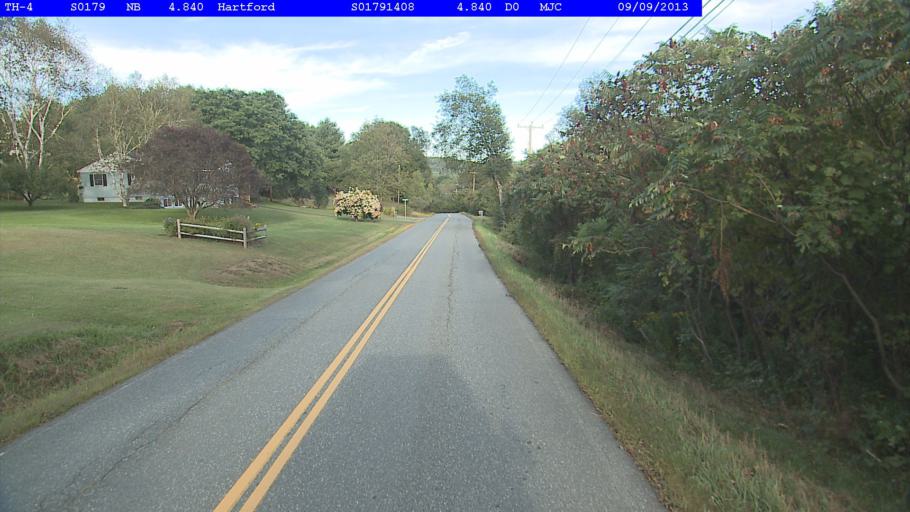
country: US
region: Vermont
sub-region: Windsor County
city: White River Junction
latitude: 43.7006
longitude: -72.4220
